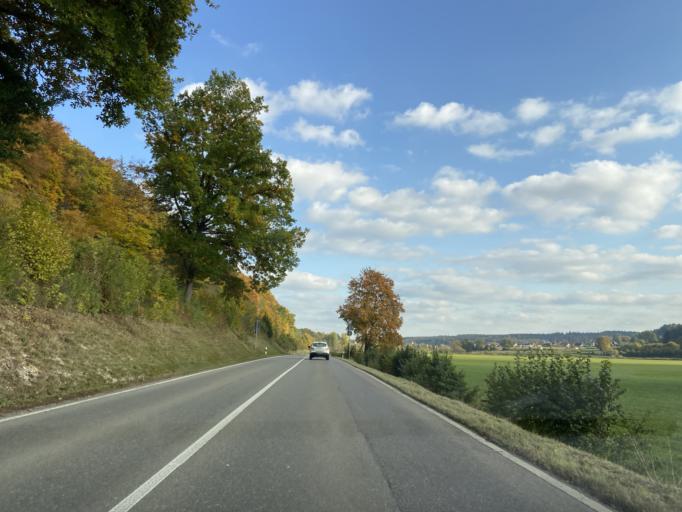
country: DE
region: Baden-Wuerttemberg
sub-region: Tuebingen Region
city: Sigmaringen
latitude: 48.0762
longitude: 9.2423
